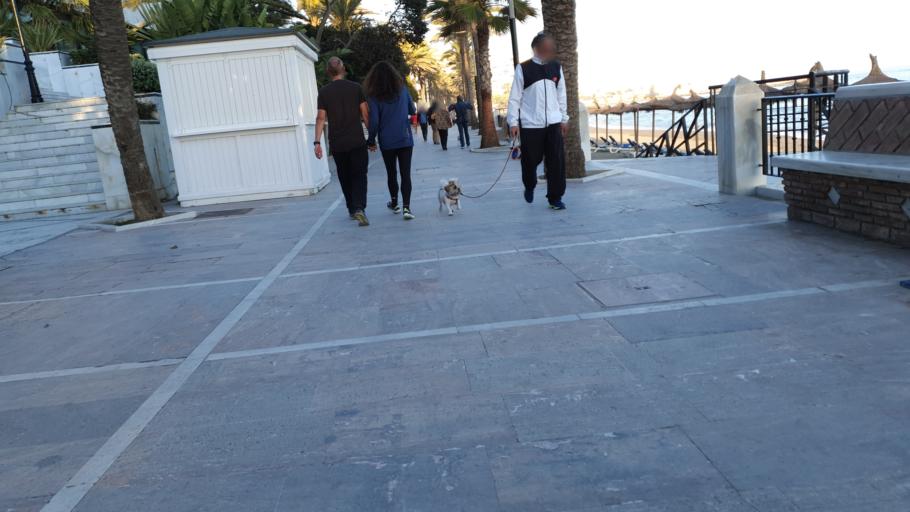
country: ES
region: Andalusia
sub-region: Provincia de Malaga
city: Marbella
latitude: 36.5069
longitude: -4.8997
